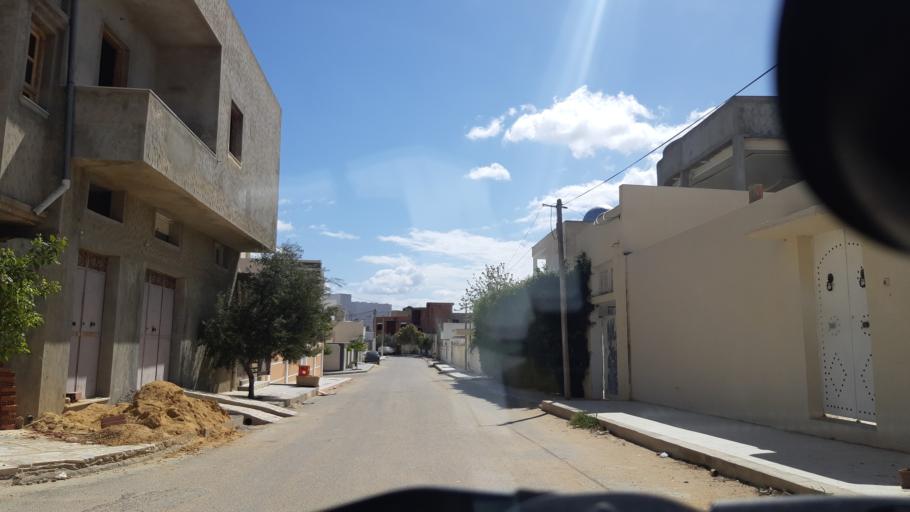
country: TN
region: Susah
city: Akouda
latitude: 35.8917
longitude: 10.5313
